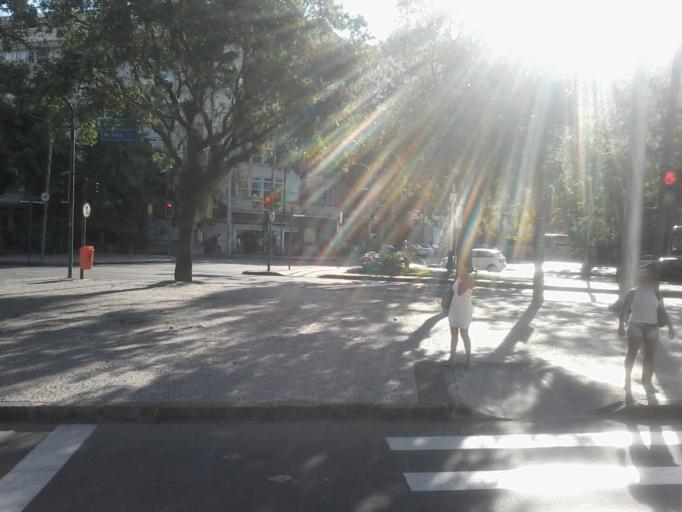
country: BR
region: Rio de Janeiro
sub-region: Rio De Janeiro
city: Rio de Janeiro
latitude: -22.9749
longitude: -43.2259
